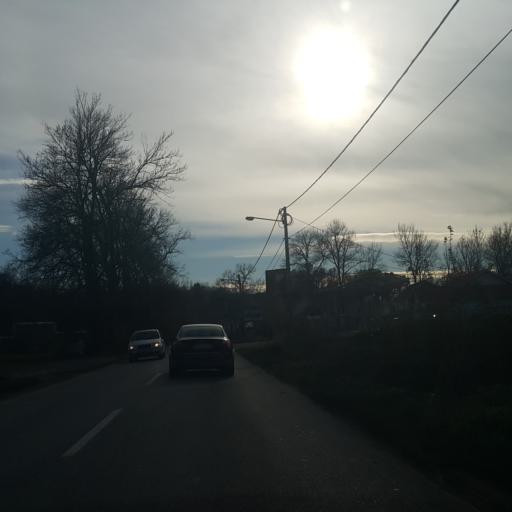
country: RS
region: Central Serbia
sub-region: Belgrade
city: Lazarevac
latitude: 44.4075
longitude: 20.2648
